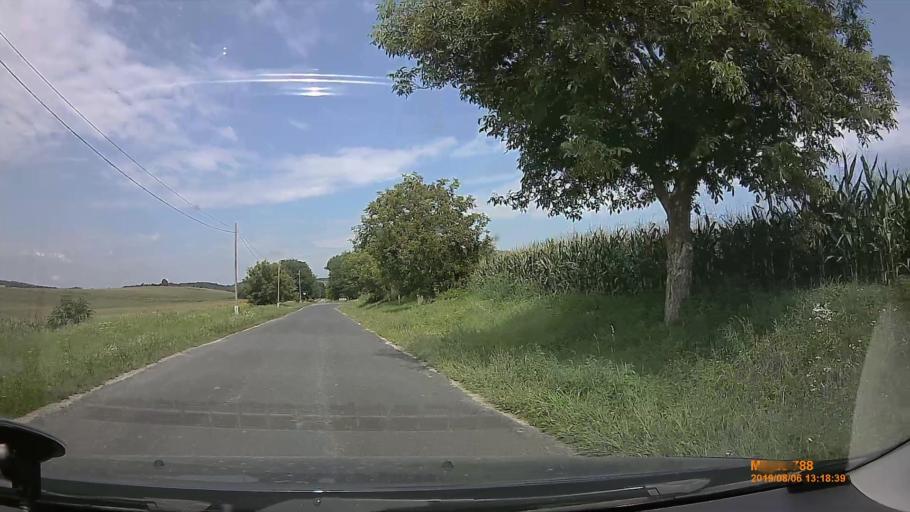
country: HU
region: Zala
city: Pacsa
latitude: 46.6345
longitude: 17.0614
